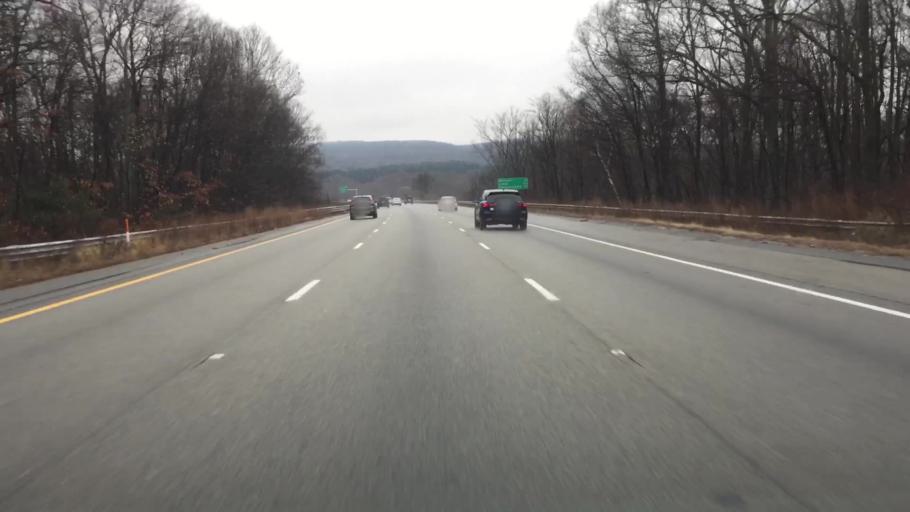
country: US
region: Massachusetts
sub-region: Worcester County
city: Southborough
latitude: 42.3000
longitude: -71.5651
